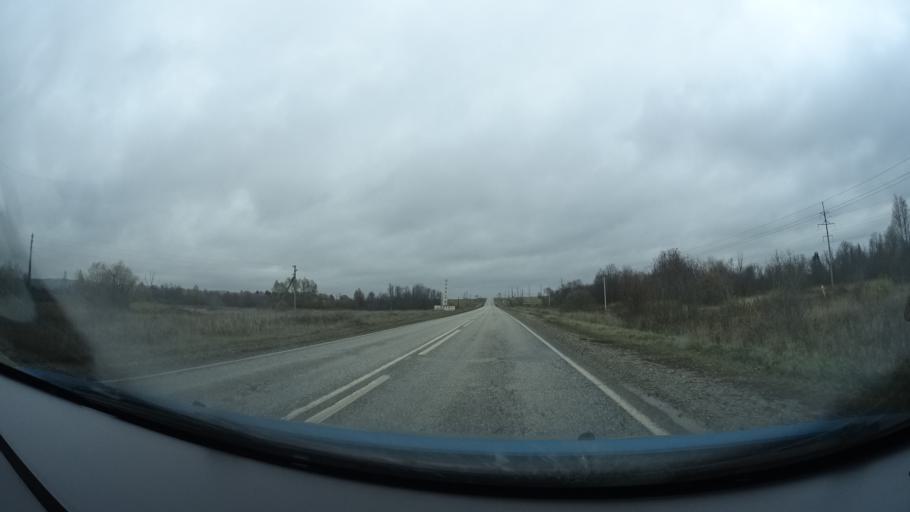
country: RU
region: Perm
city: Osa
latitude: 57.1086
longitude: 55.5231
